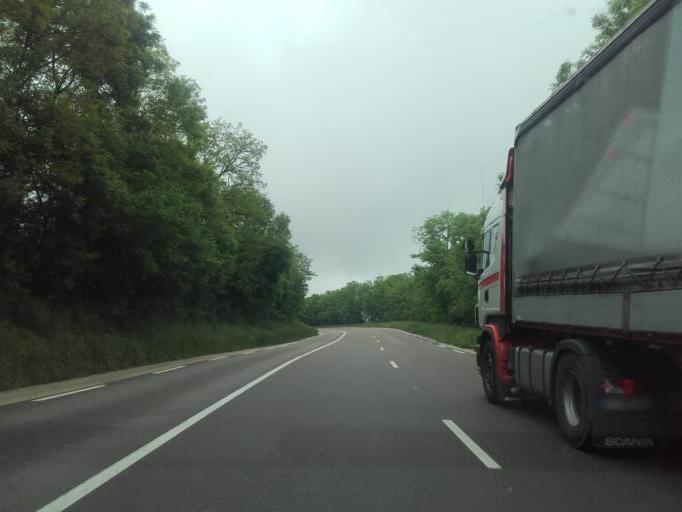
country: FR
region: Bourgogne
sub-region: Departement de la Cote-d'Or
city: Nolay
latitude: 46.9622
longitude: 4.6746
